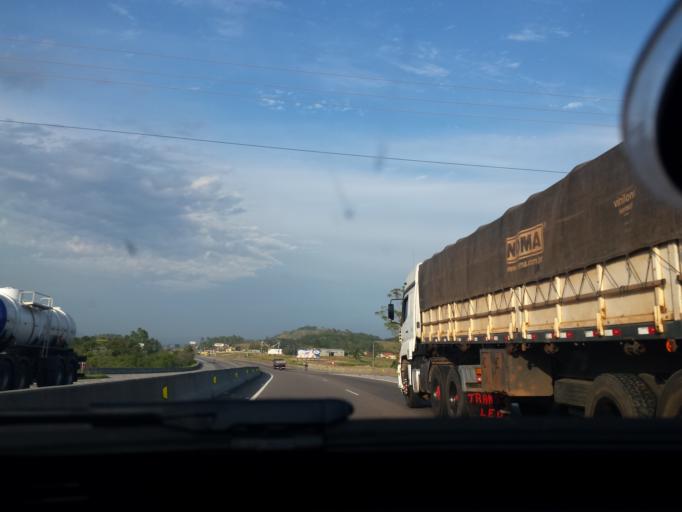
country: BR
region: Santa Catarina
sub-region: Tubarao
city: Tubarao
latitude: -28.4245
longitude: -48.9002
